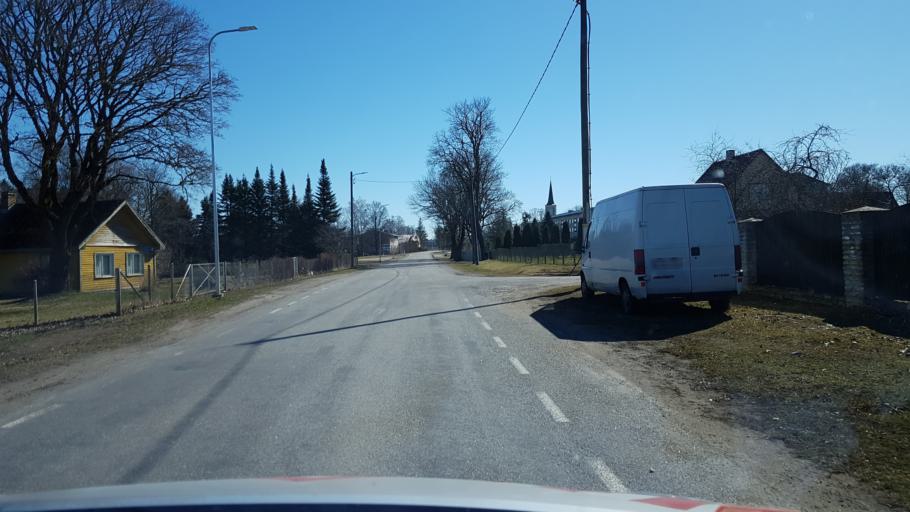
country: EE
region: Laeaene-Virumaa
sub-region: Haljala vald
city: Haljala
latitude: 59.4337
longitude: 26.2586
